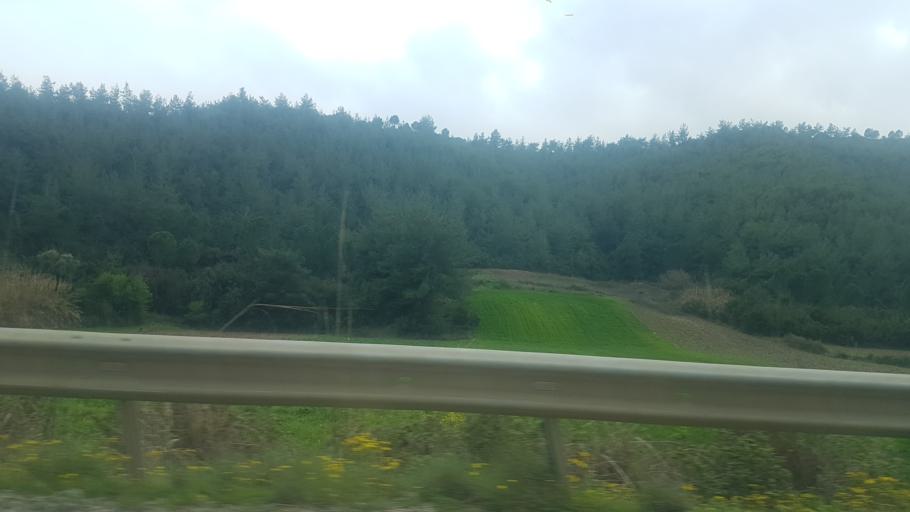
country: TR
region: Mersin
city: Yenice
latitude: 37.0917
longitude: 35.1386
